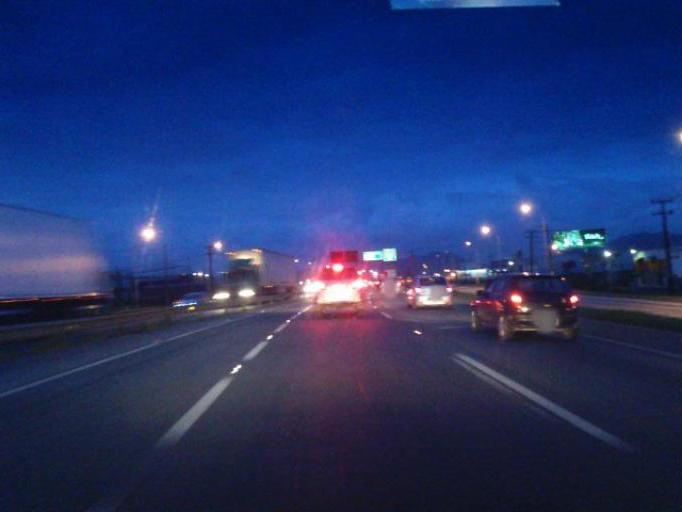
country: BR
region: Santa Catarina
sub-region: Itajai
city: Itajai
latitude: -26.8563
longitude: -48.7273
